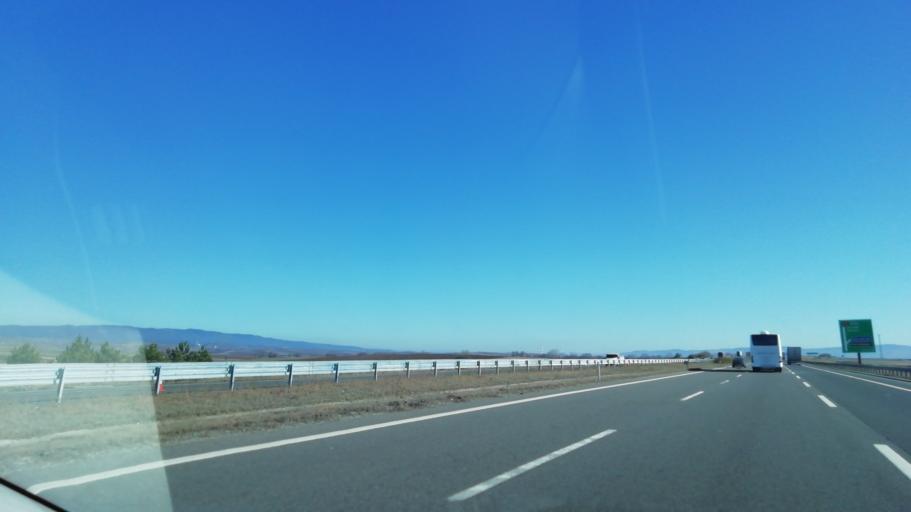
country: TR
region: Bolu
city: Dortdivan
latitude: 40.7466
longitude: 32.0991
